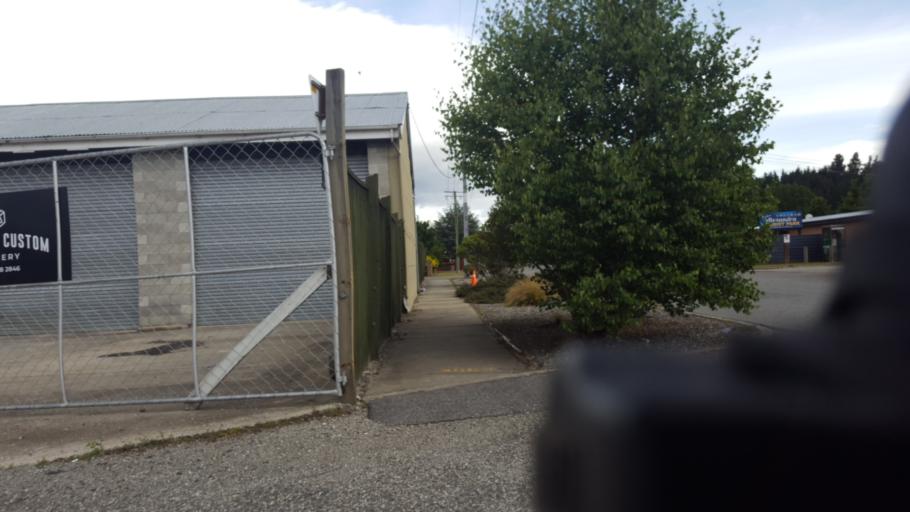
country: NZ
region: Otago
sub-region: Queenstown-Lakes District
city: Wanaka
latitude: -45.2437
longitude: 169.3953
